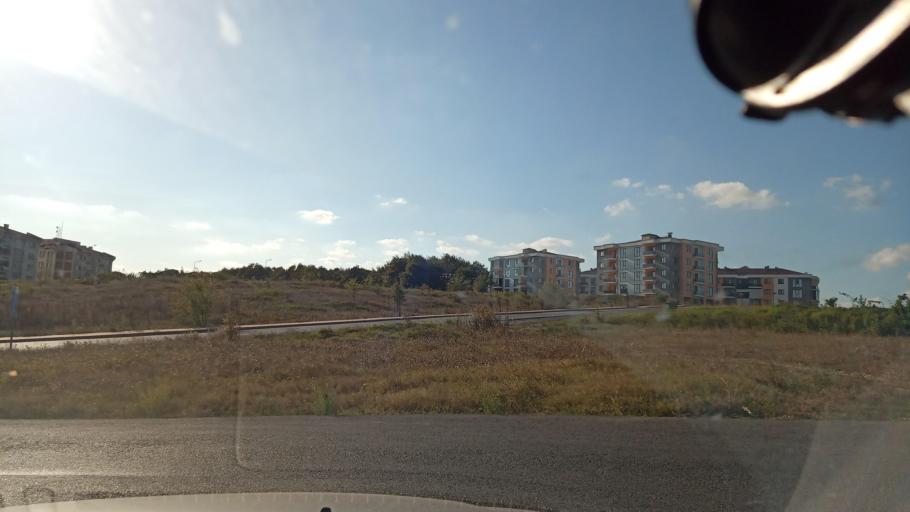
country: TR
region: Kocaeli
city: Kaymaz
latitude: 40.8610
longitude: 30.2775
